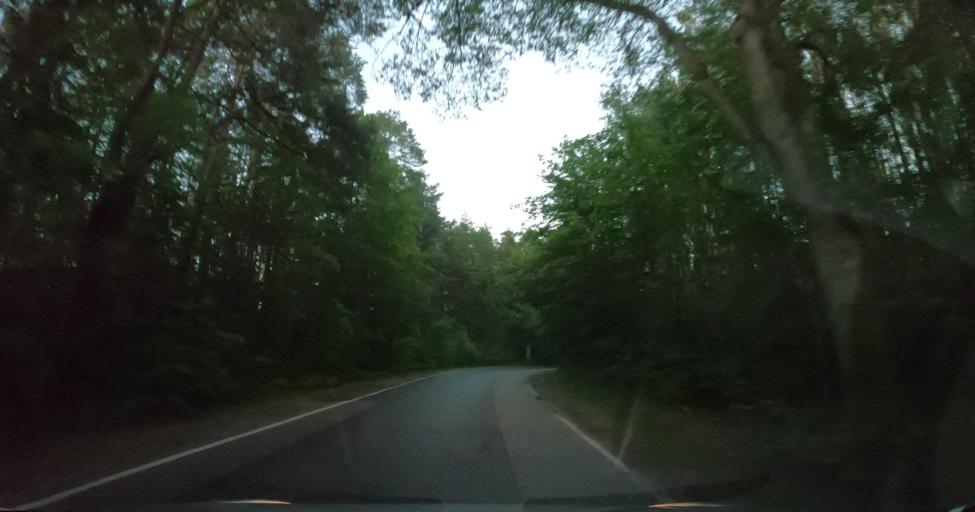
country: PL
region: Pomeranian Voivodeship
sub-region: Powiat wejherowski
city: Luzino
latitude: 54.4657
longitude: 18.1143
